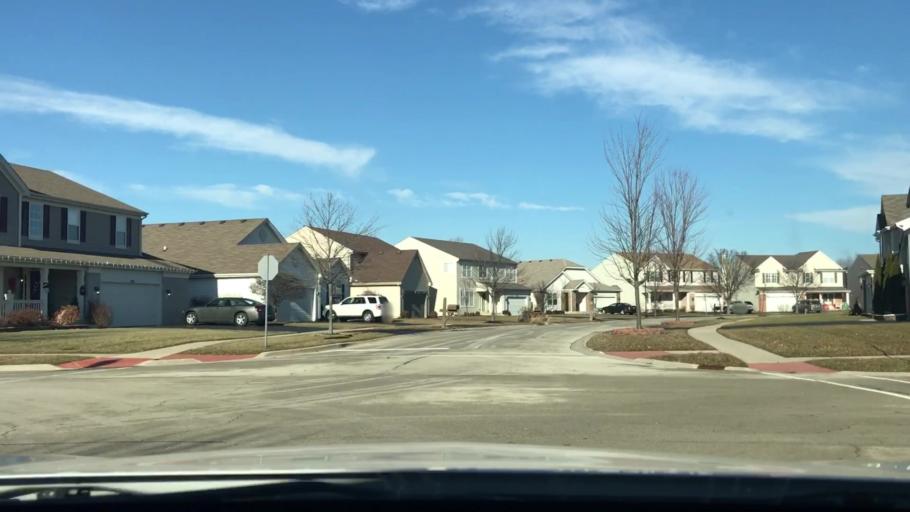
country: US
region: Illinois
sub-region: Kane County
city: Pingree Grove
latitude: 42.0870
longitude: -88.4502
